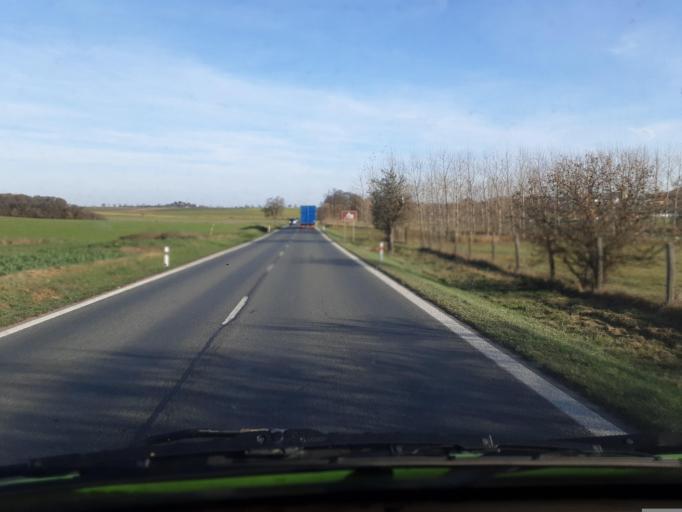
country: CZ
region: Plzensky
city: Horazd'ovice
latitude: 49.3288
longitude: 13.6681
